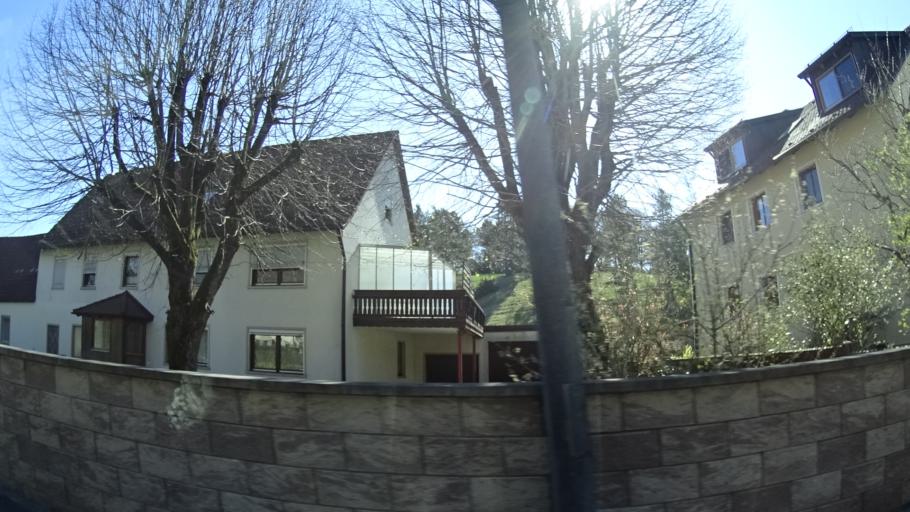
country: DE
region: Bavaria
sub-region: Regierungsbezirk Mittelfranken
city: Alfeld
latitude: 49.4260
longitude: 11.5442
